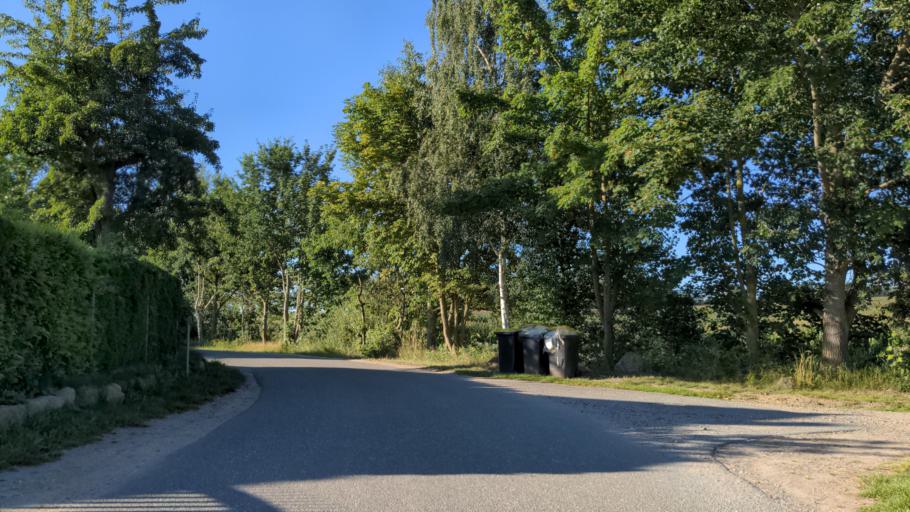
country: DE
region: Mecklenburg-Vorpommern
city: Kalkhorst
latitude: 53.9581
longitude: 11.0083
